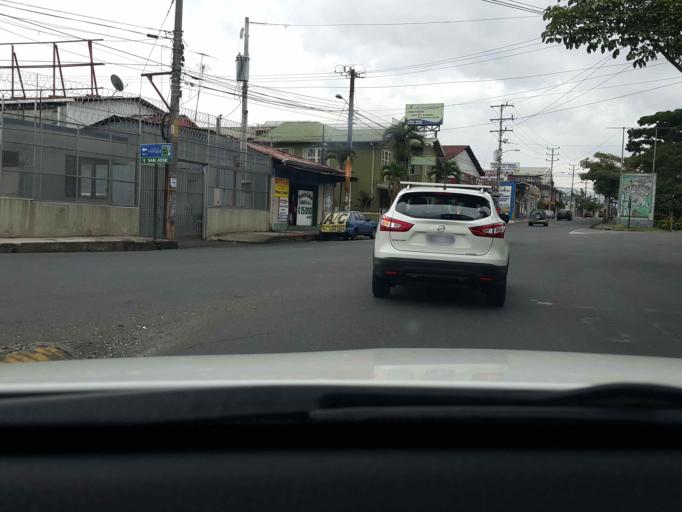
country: CR
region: San Jose
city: San Jose
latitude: 9.9329
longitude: -84.0979
